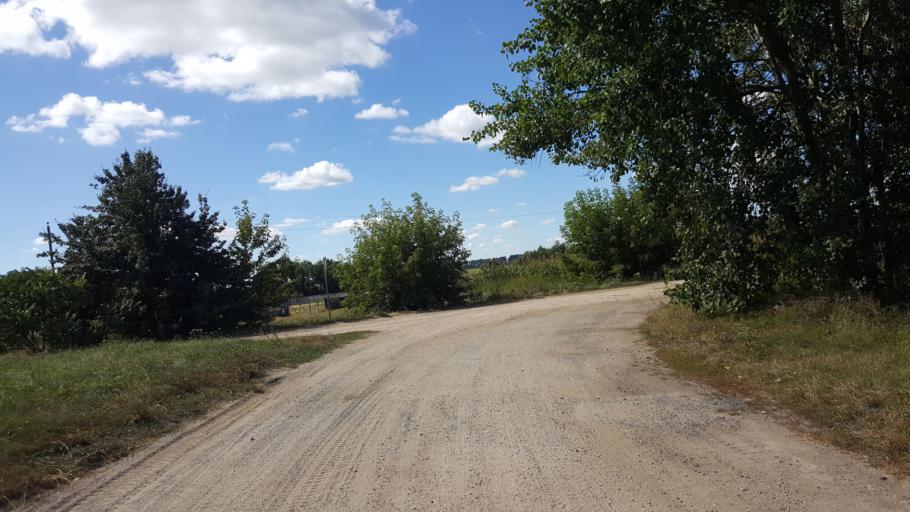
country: BY
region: Brest
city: Vysokaye
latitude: 52.2918
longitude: 23.3000
